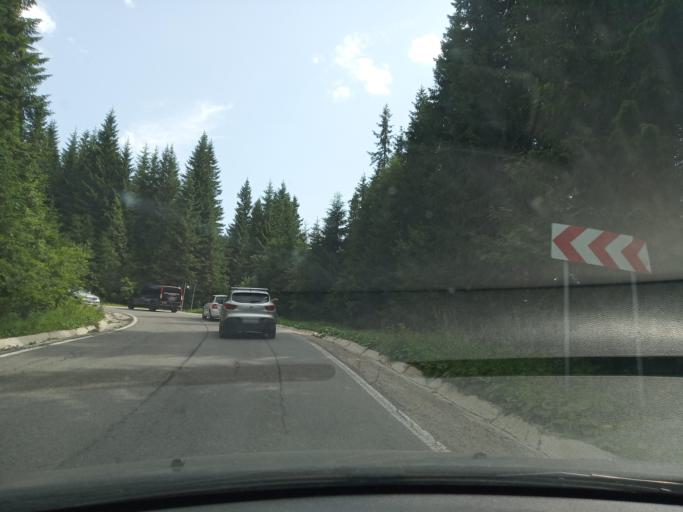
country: RO
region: Dambovita
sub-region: Comuna Moroeni
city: Glod
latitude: 45.3255
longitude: 25.4367
